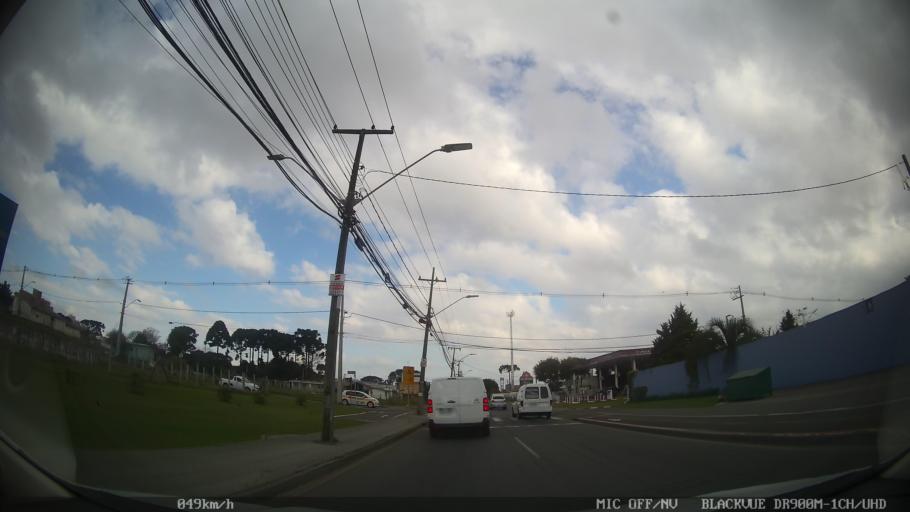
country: BR
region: Parana
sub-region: Pinhais
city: Pinhais
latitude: -25.4338
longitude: -49.1937
